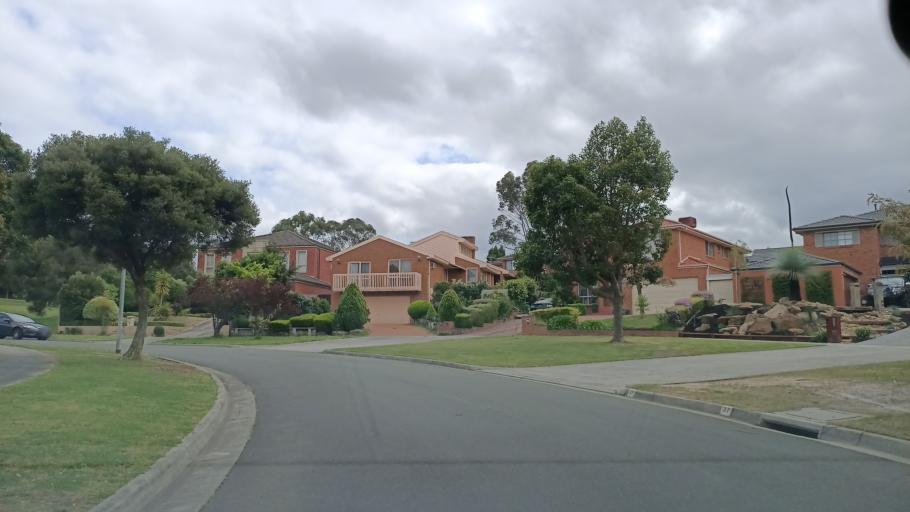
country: AU
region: Victoria
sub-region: Monash
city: Mulgrave
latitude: -37.9198
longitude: 145.1986
